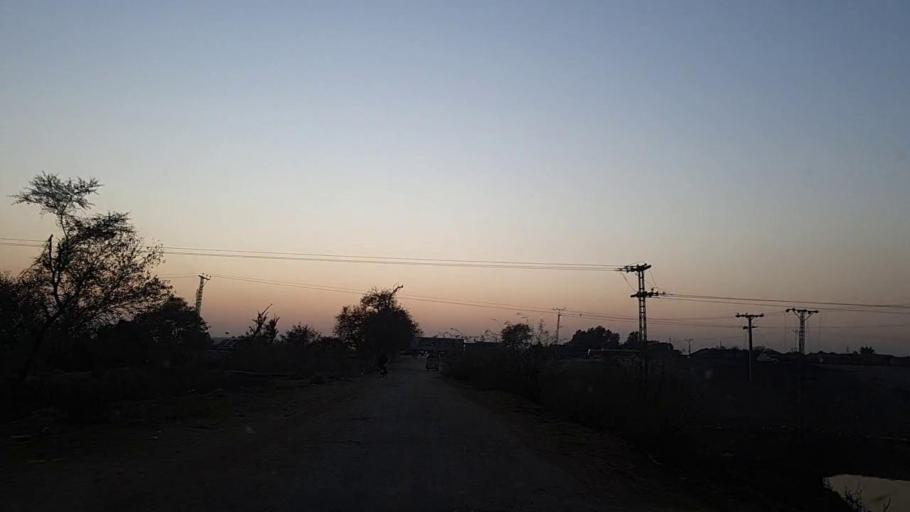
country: PK
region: Sindh
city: Hala
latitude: 25.9585
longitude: 68.3843
